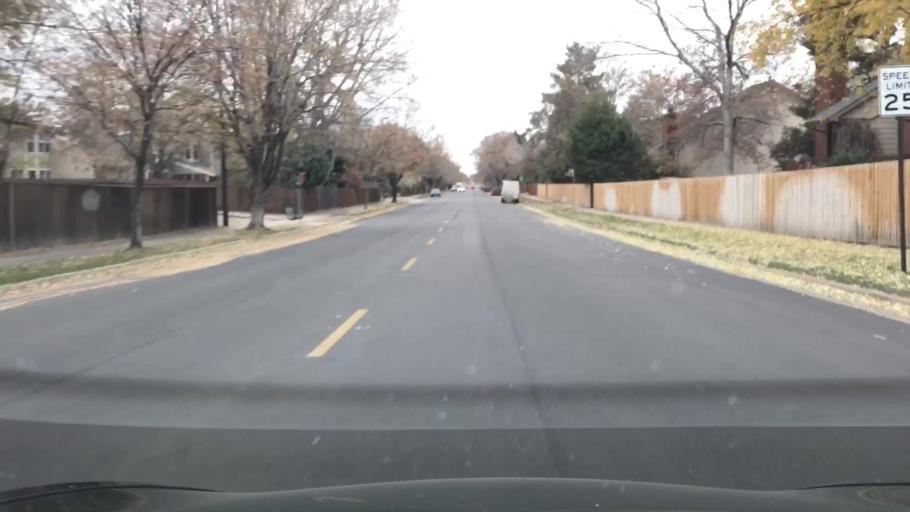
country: US
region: Colorado
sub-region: Arapahoe County
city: Glendale
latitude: 39.6894
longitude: -104.8973
